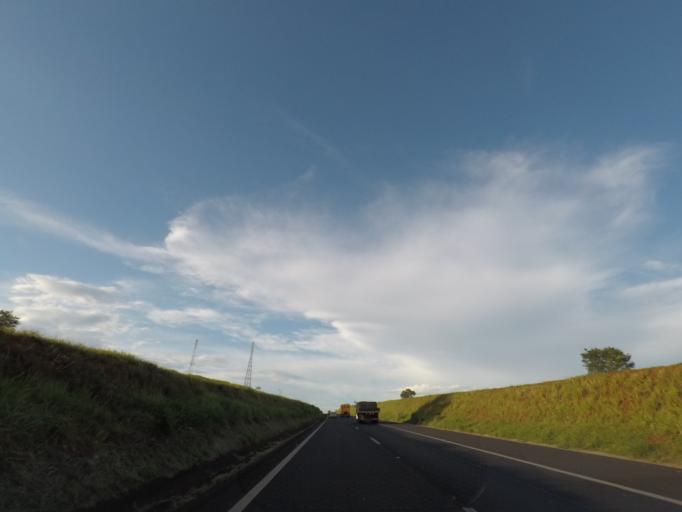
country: BR
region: Sao Paulo
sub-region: Ituverava
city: Ituverava
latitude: -20.2739
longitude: -47.7977
